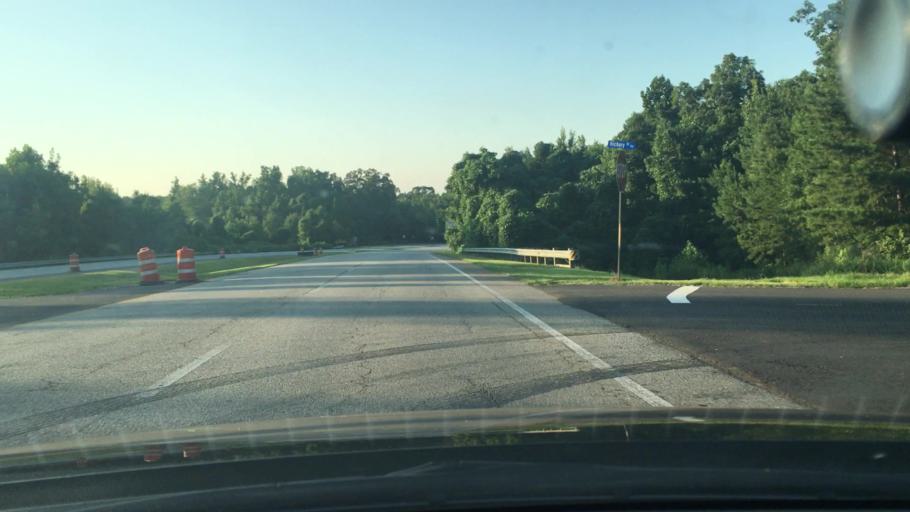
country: US
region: Georgia
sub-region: Coweta County
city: East Newnan
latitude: 33.3633
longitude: -84.7656
